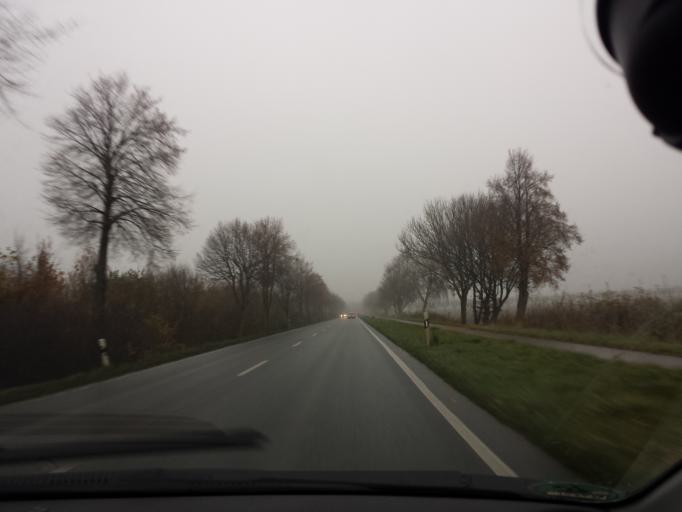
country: DE
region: North Rhine-Westphalia
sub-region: Regierungsbezirk Koln
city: Ubach-Palenberg
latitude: 50.9450
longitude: 6.1310
